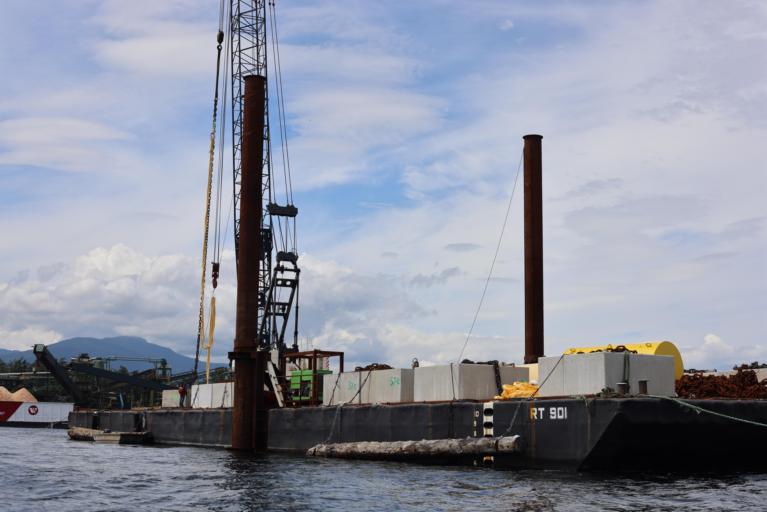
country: CA
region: British Columbia
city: Nanaimo
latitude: 49.1564
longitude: -123.8831
